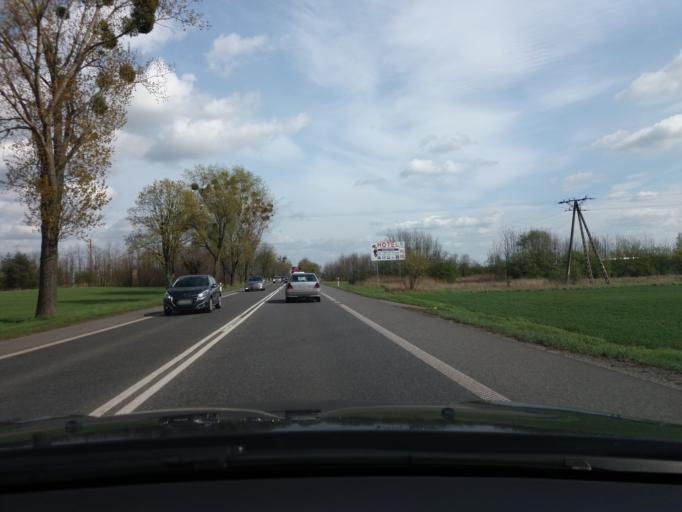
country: PL
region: Lower Silesian Voivodeship
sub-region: Powiat sredzki
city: Mrozow
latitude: 51.1568
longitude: 16.7985
